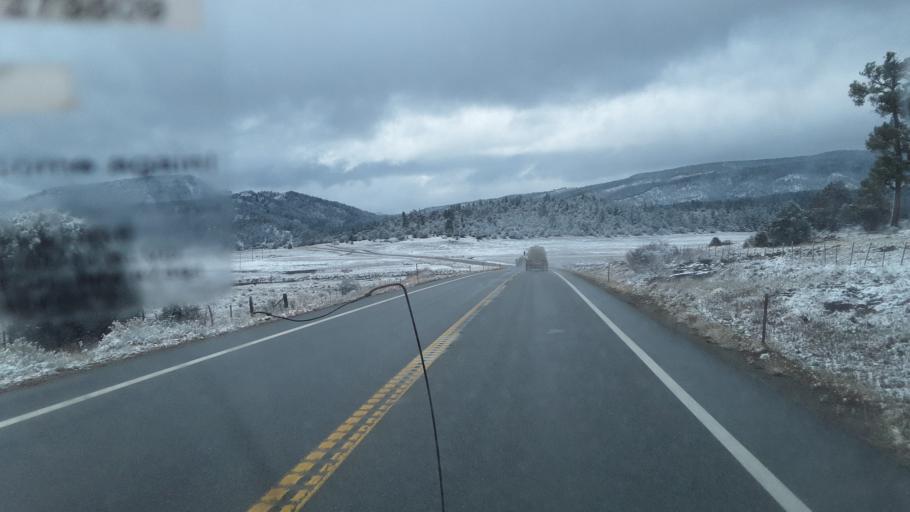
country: US
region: Colorado
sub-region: Archuleta County
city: Pagosa Springs
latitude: 37.2289
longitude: -107.1961
